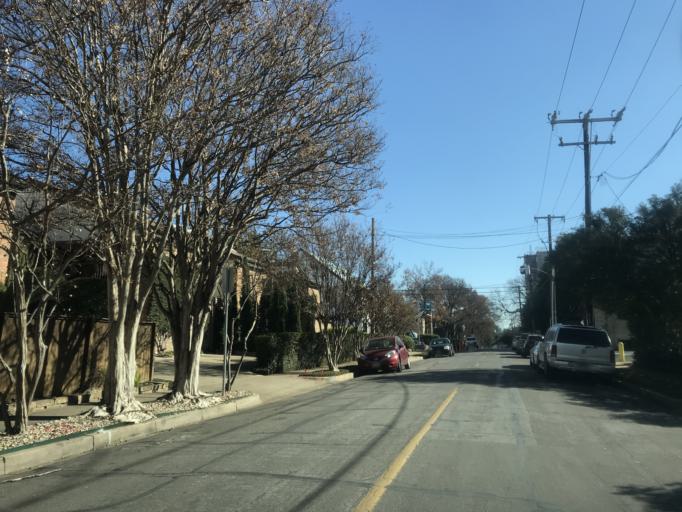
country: US
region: Texas
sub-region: Dallas County
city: Highland Park
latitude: 32.8203
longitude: -96.7920
